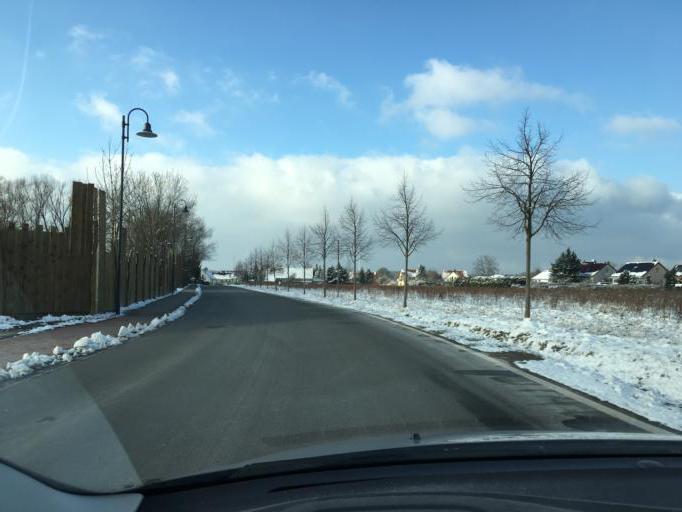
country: DE
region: Saxony
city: Grimma
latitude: 51.2579
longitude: 12.6920
